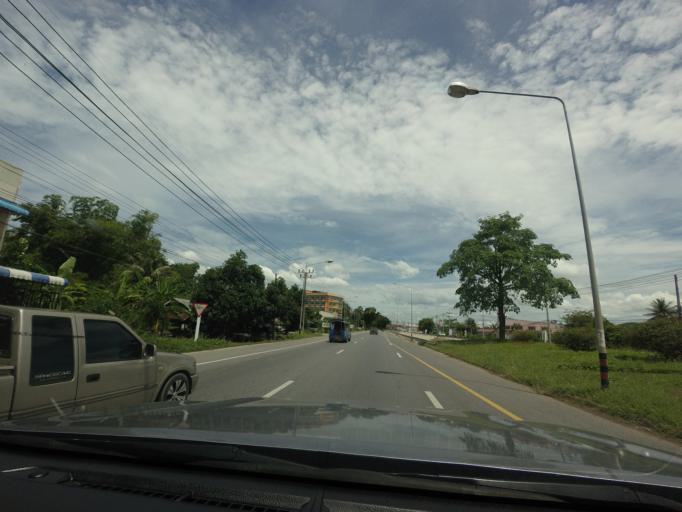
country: TH
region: Songkhla
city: Ban Mai
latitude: 7.2129
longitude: 100.5570
